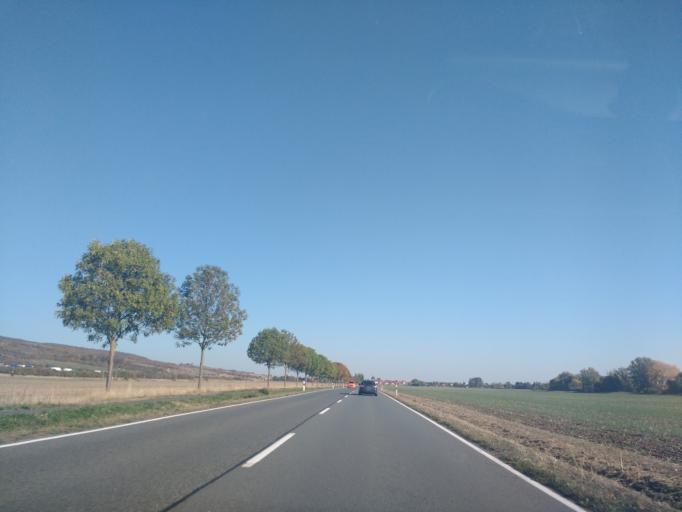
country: DE
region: Saxony-Anhalt
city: Bennungen
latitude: 51.4594
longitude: 11.1457
